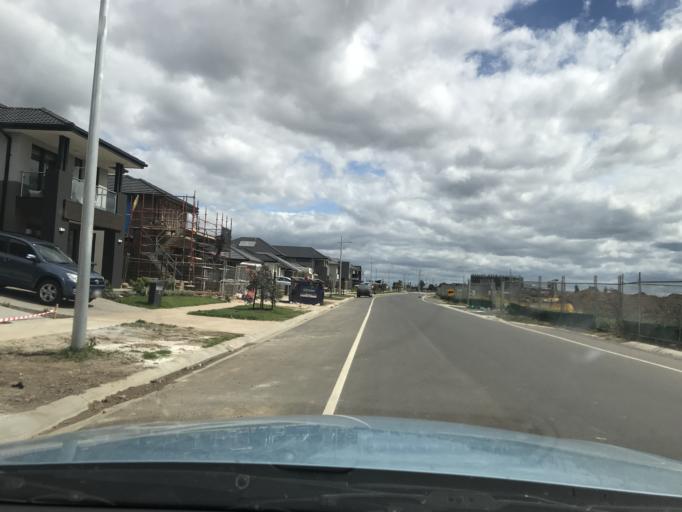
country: AU
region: Victoria
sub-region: Wyndham
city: Williams Landing
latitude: -37.8660
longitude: 144.7528
